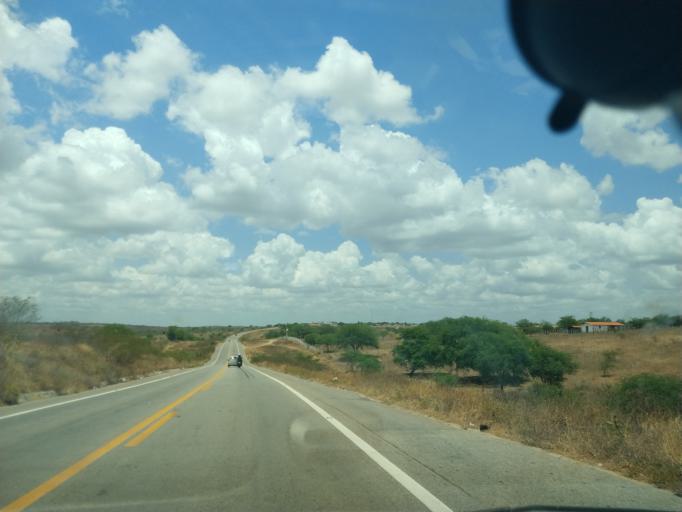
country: BR
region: Rio Grande do Norte
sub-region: Tangara
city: Tangara
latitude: -6.1841
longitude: -35.7758
